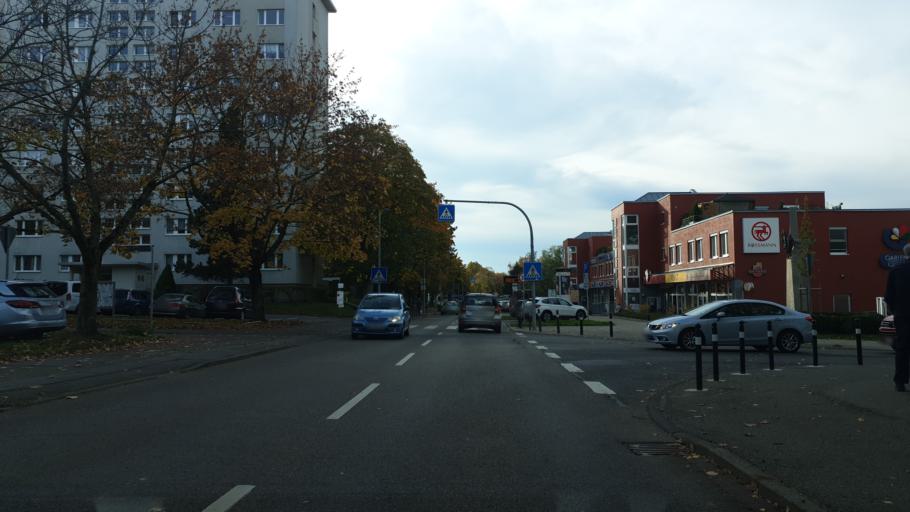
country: DE
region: Saxony
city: Hilbersdorf
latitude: 50.8221
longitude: 12.9608
